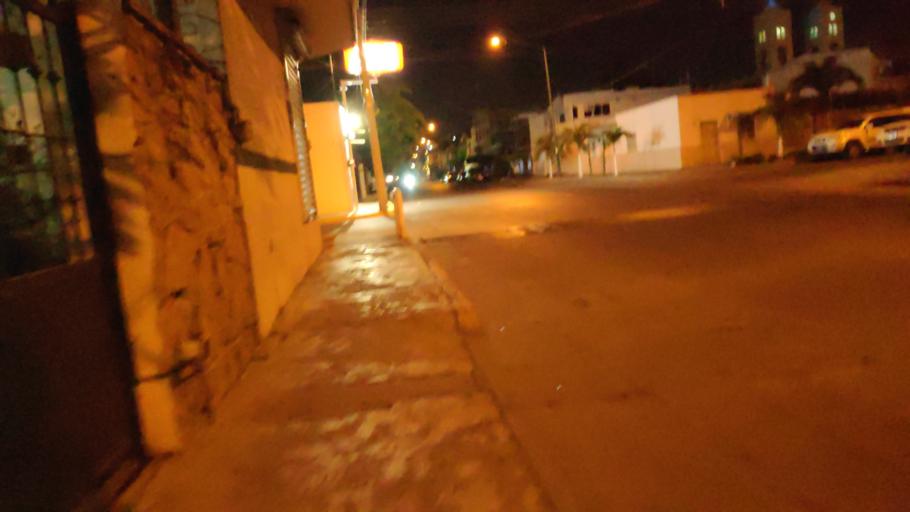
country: MX
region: Sinaloa
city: Culiacan
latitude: 24.7921
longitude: -107.4092
